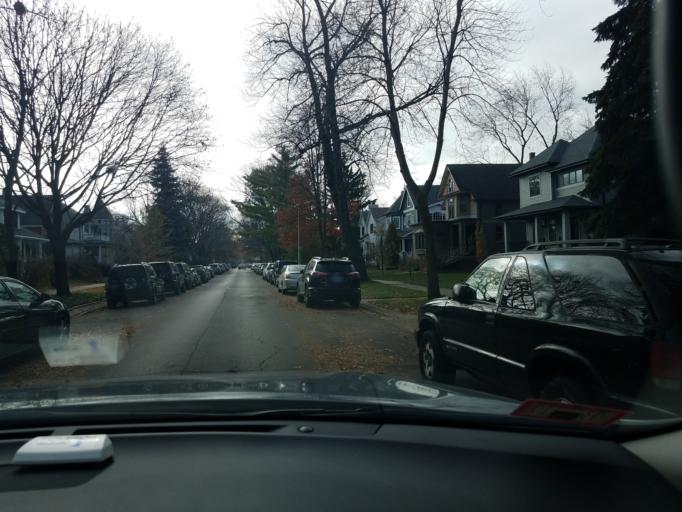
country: US
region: Illinois
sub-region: Cook County
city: Lincolnwood
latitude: 41.9513
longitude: -87.7339
